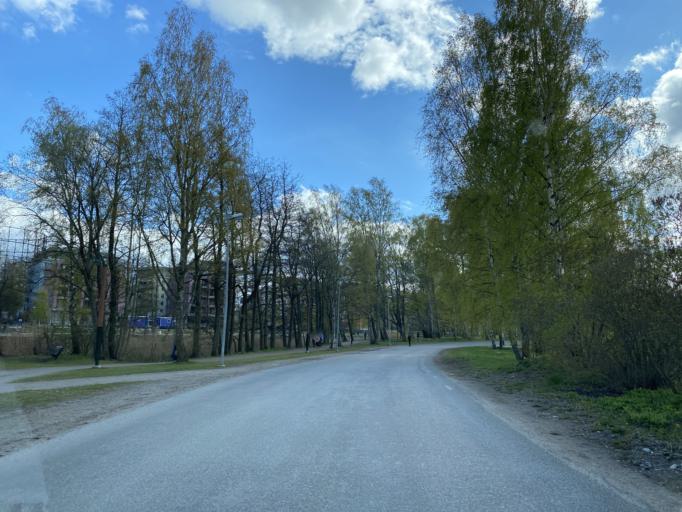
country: SE
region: Stockholm
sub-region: Stockholms Kommun
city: OEstermalm
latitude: 59.3595
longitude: 18.0859
